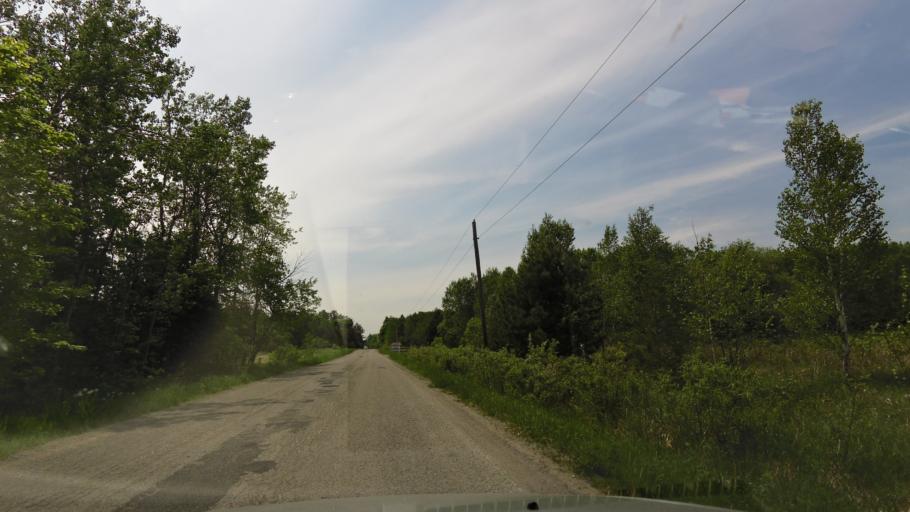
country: CA
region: Ontario
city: Cobourg
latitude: 43.9805
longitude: -78.4797
